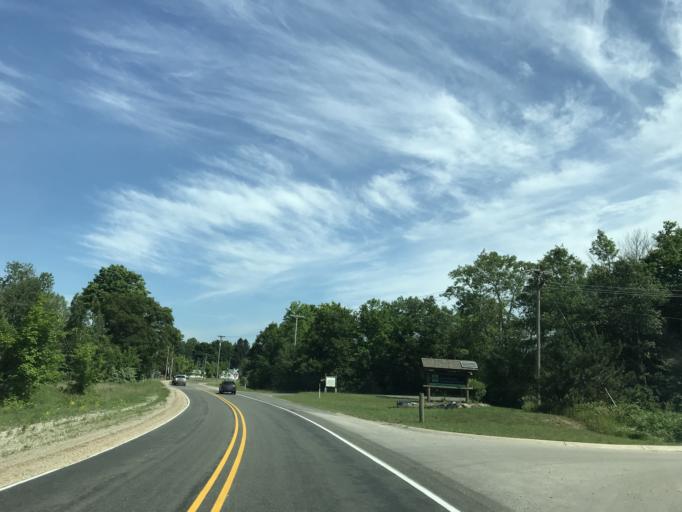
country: US
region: Michigan
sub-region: Grand Traverse County
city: Traverse City
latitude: 44.7078
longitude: -85.6259
